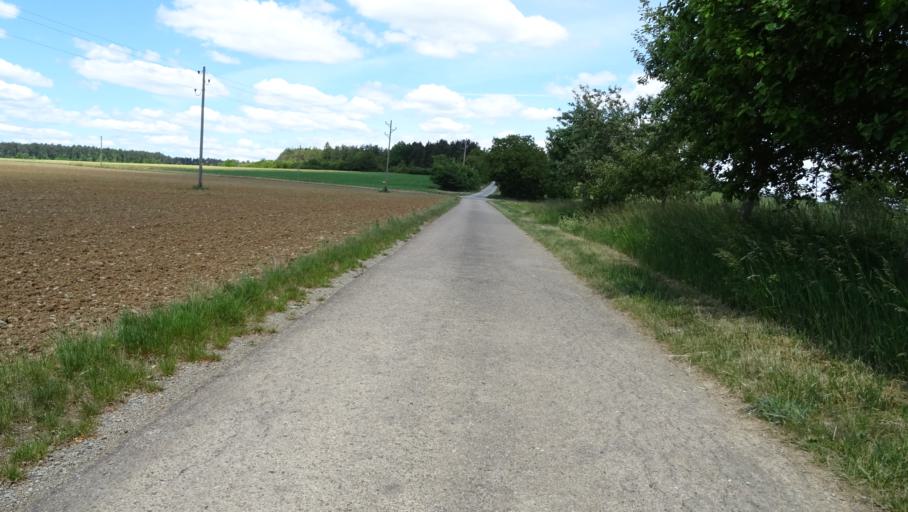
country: DE
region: Baden-Wuerttemberg
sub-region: Karlsruhe Region
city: Seckach
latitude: 49.4695
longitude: 9.3318
